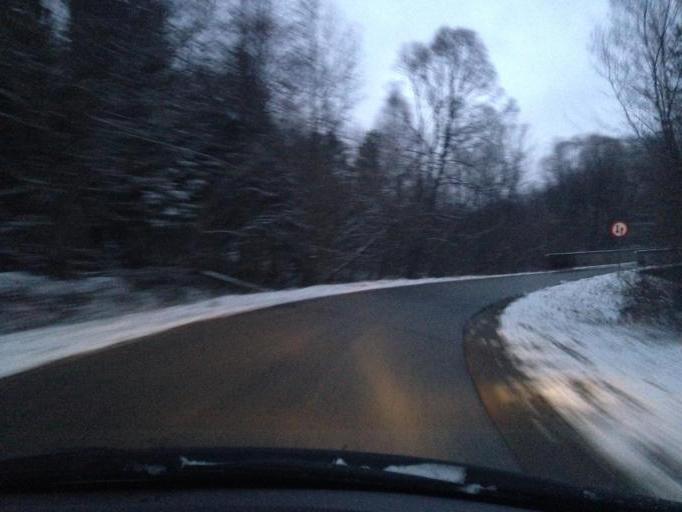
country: PL
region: Subcarpathian Voivodeship
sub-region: Powiat jasielski
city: Krempna
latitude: 49.5158
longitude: 21.5415
